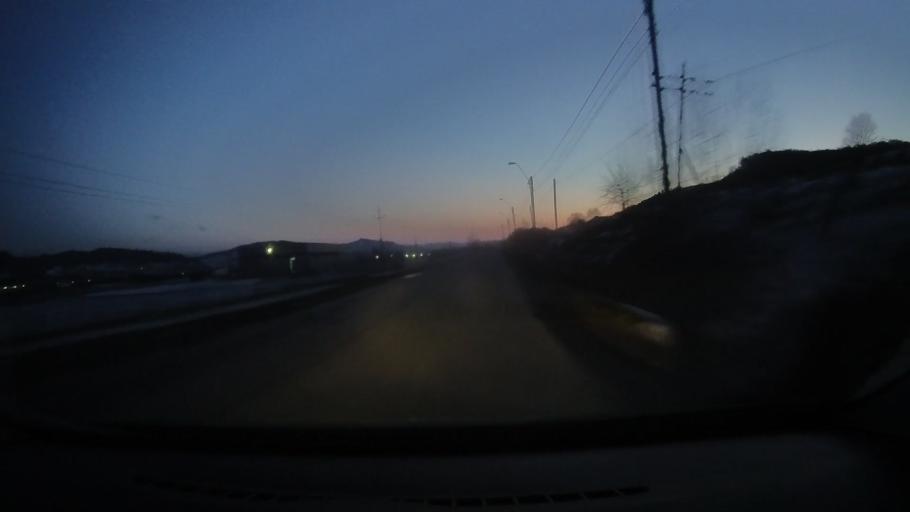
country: RO
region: Sibiu
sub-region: Municipiul Medias
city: Medias
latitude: 46.1799
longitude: 24.3687
